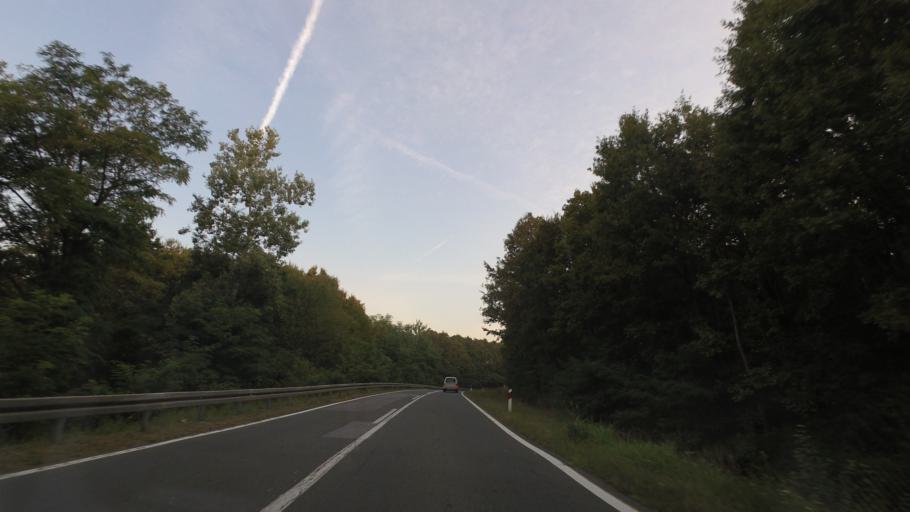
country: HR
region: Brodsko-Posavska
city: Cernik
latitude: 45.2759
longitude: 17.4027
